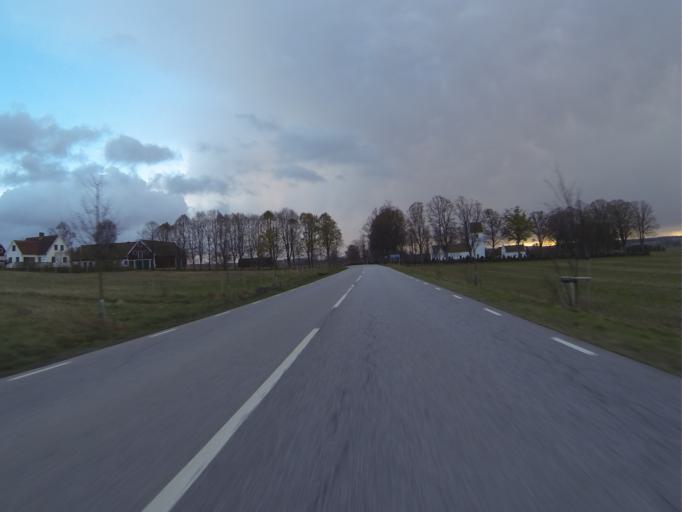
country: SE
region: Skane
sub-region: Lunds Kommun
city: Genarp
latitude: 55.6162
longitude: 13.4053
